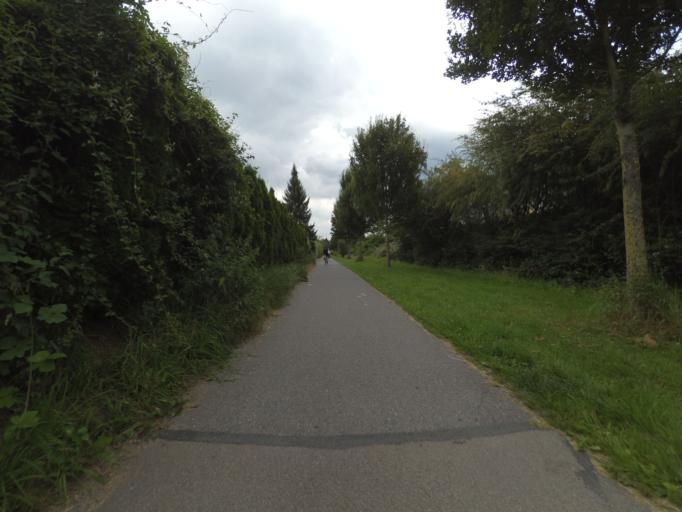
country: DE
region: North Rhine-Westphalia
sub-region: Regierungsbezirk Koln
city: Wurselen
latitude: 50.7449
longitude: 6.1515
